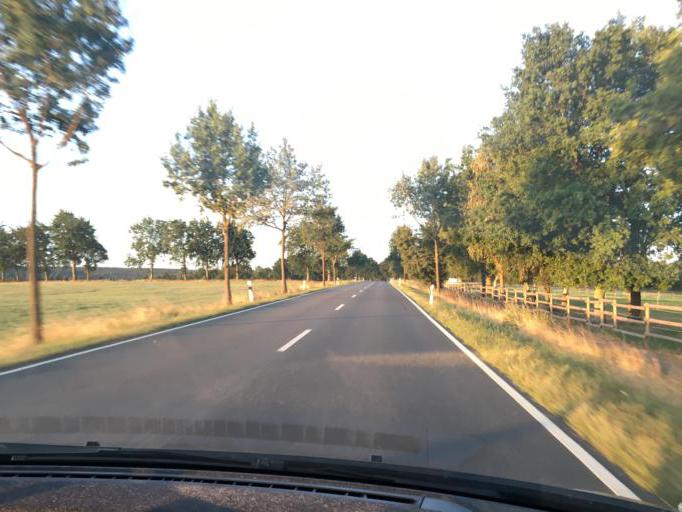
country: DE
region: North Rhine-Westphalia
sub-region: Regierungsbezirk Koln
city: Hurtgenwald
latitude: 50.6720
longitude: 6.3452
